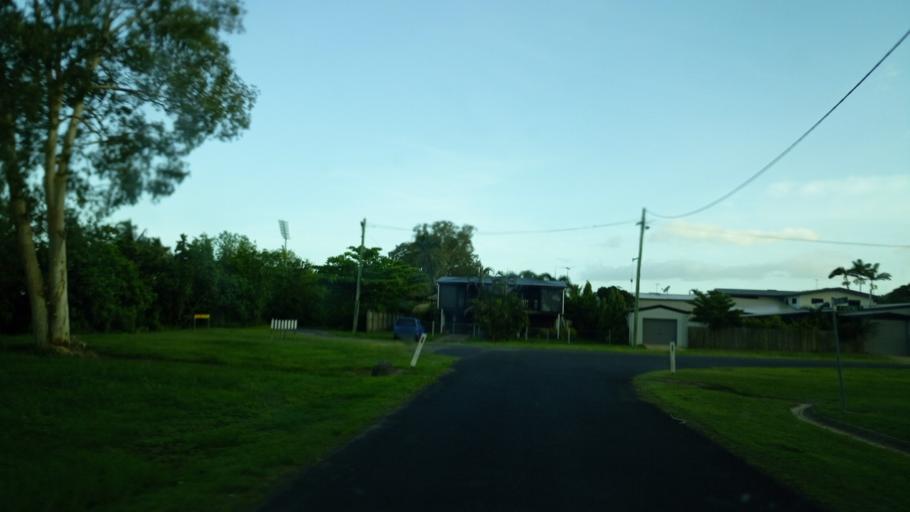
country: AU
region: Queensland
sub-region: Cairns
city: Woree
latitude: -16.9343
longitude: 145.7453
